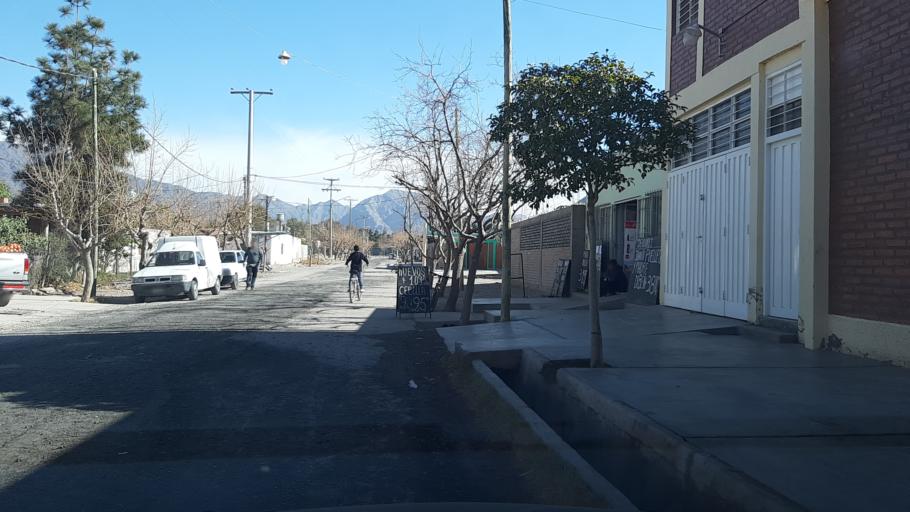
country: AR
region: San Juan
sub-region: Departamento de Zonda
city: Zonda
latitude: -31.5486
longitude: -68.7296
